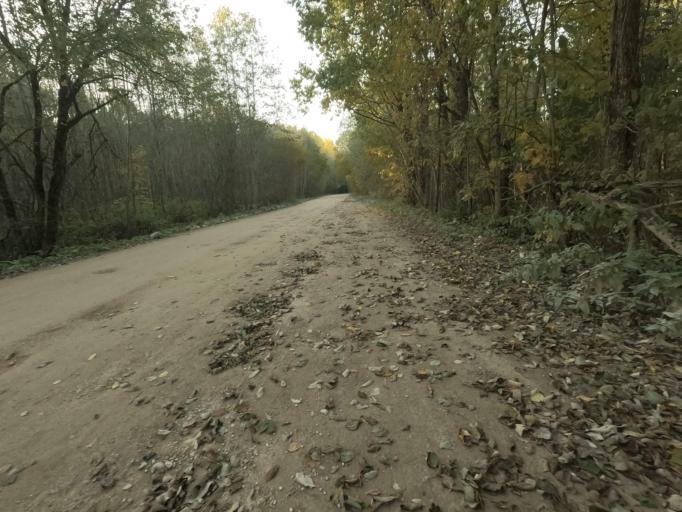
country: RU
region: Leningrad
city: Lyuban'
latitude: 59.0032
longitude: 31.0975
